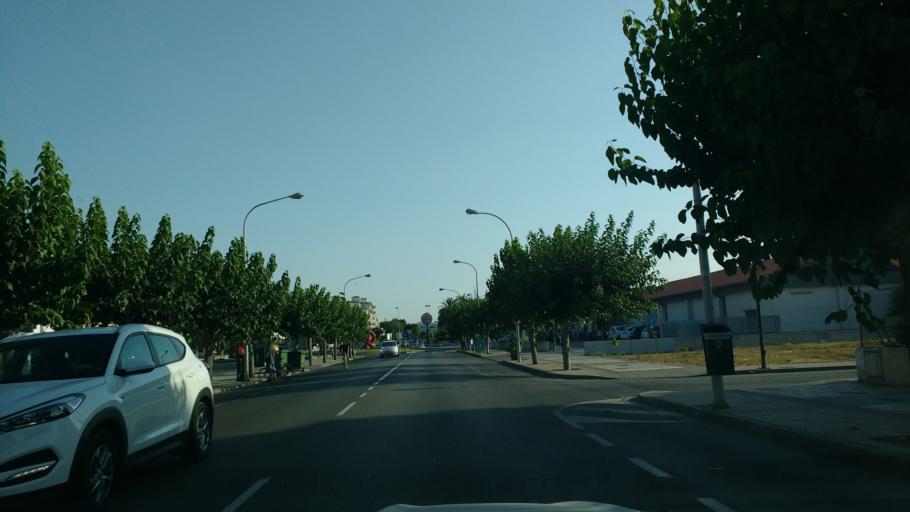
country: ES
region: Balearic Islands
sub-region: Illes Balears
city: Port d'Alcudia
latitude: 39.8409
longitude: 3.1216
